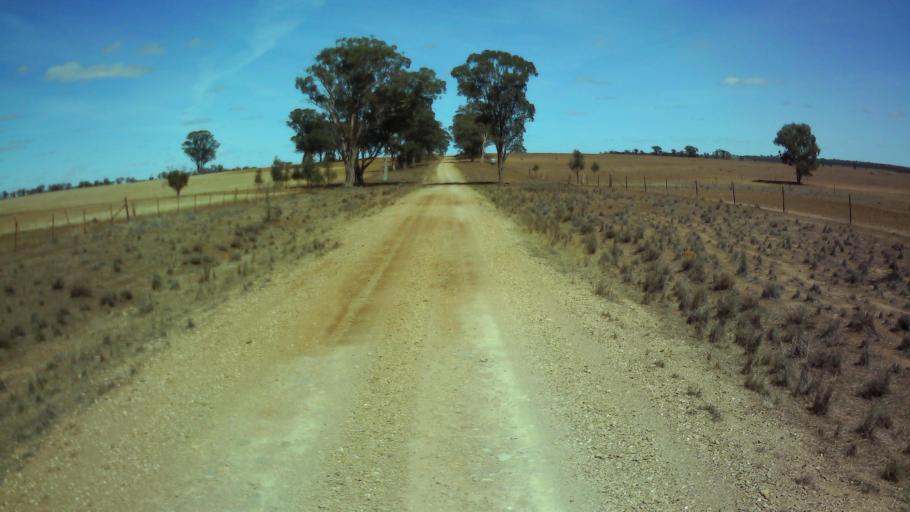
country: AU
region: New South Wales
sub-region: Weddin
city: Grenfell
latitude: -33.7255
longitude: 147.8710
